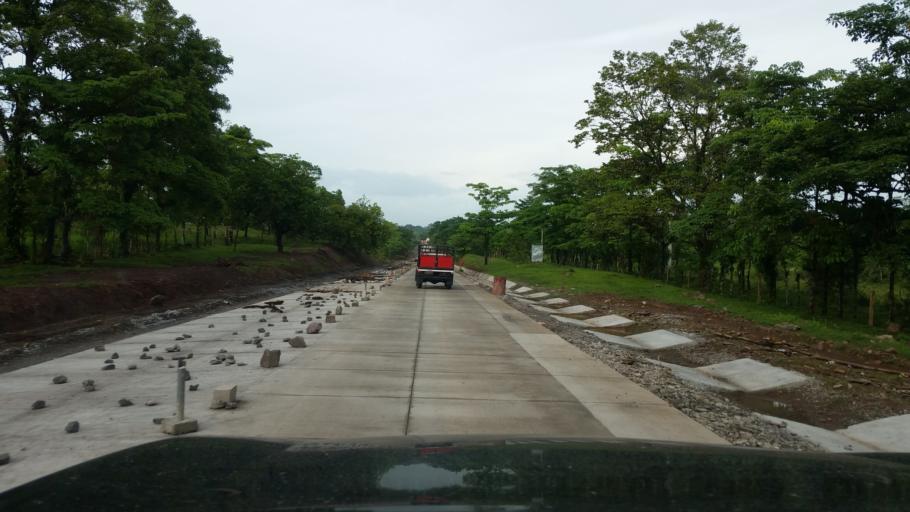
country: NI
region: Matagalpa
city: Rio Blanco
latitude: 13.0700
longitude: -85.0723
